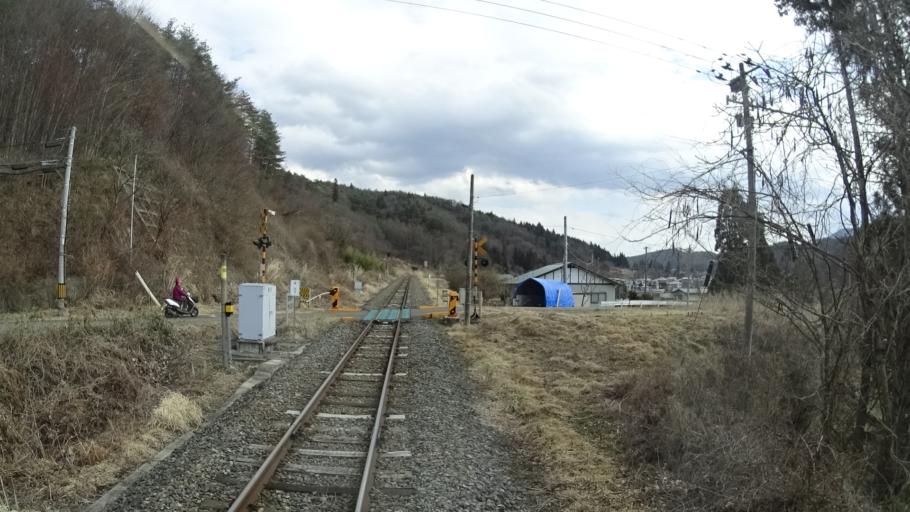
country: JP
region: Iwate
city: Tono
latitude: 39.3539
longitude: 141.3477
